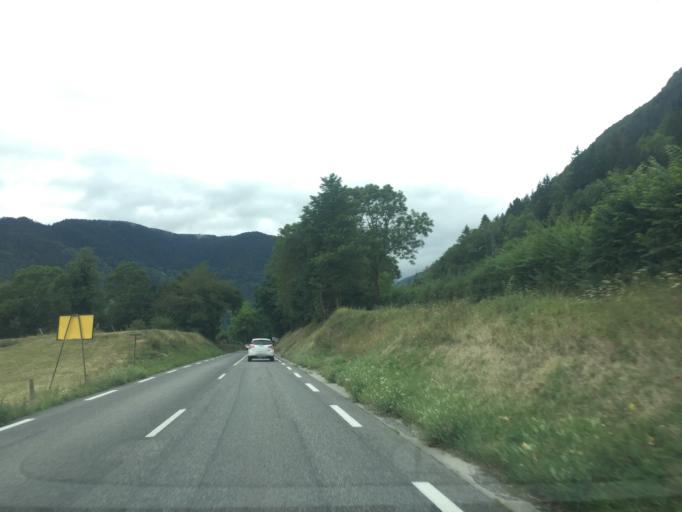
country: FR
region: Midi-Pyrenees
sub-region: Departement des Hautes-Pyrenees
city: Saint-Lary-Soulan
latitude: 42.8596
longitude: 0.3398
